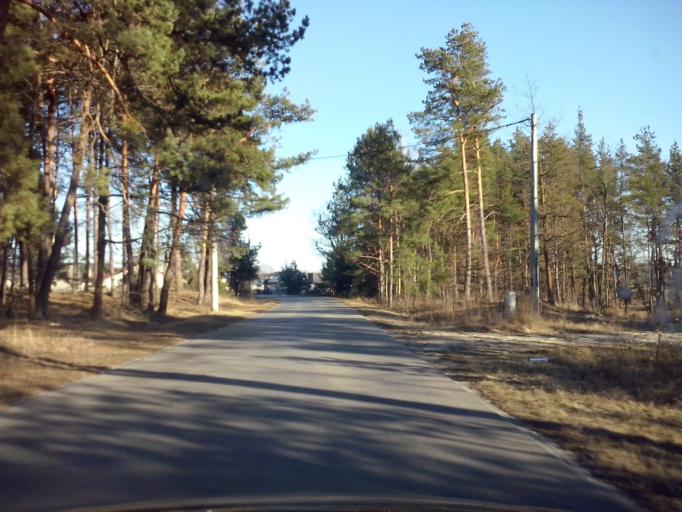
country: PL
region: Subcarpathian Voivodeship
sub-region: Powiat nizanski
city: Harasiuki
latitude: 50.5230
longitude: 22.4754
